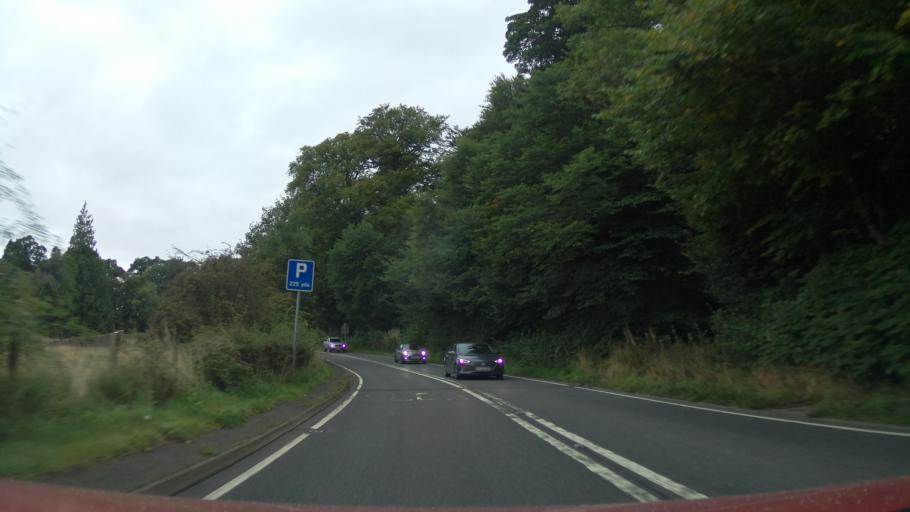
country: GB
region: Scotland
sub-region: Clackmannanshire
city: Tillicoultry
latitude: 56.1589
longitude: -3.7062
